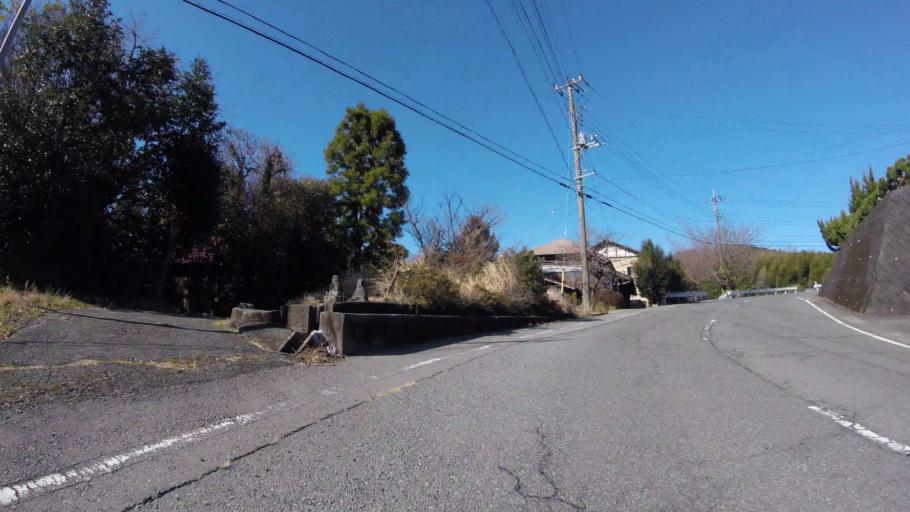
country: JP
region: Shizuoka
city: Ito
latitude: 34.8928
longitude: 138.9391
